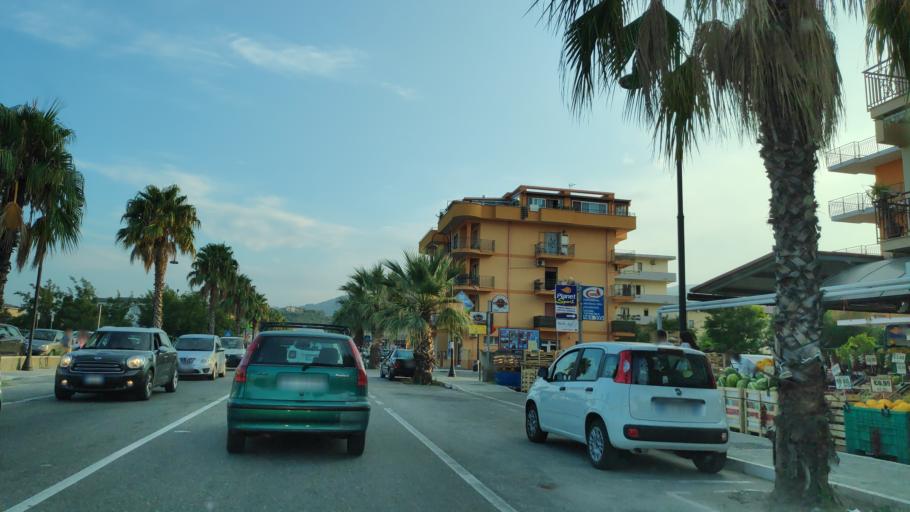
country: IT
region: Calabria
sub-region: Provincia di Catanzaro
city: Marina di Davoli
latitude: 38.6667
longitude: 16.5460
